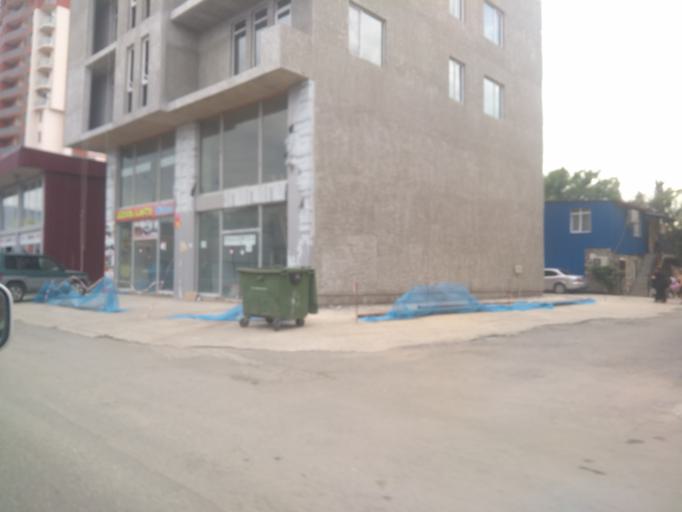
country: GE
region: Ajaria
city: Batumi
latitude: 41.6233
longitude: 41.6135
